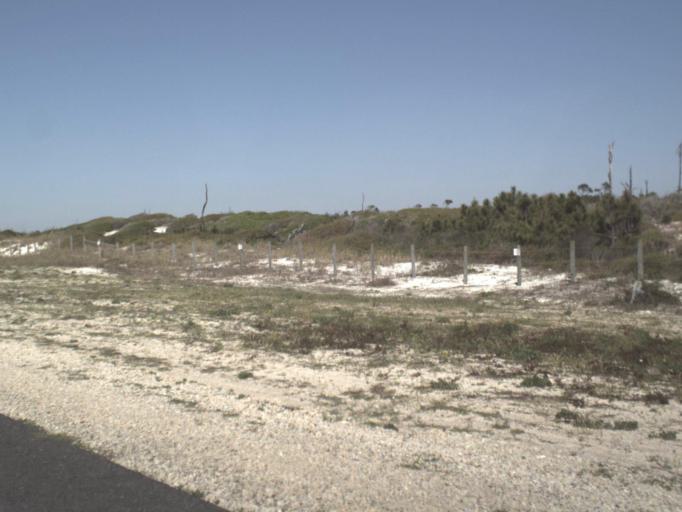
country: US
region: Florida
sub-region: Okaloosa County
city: Destin
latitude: 30.3893
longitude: -86.5307
